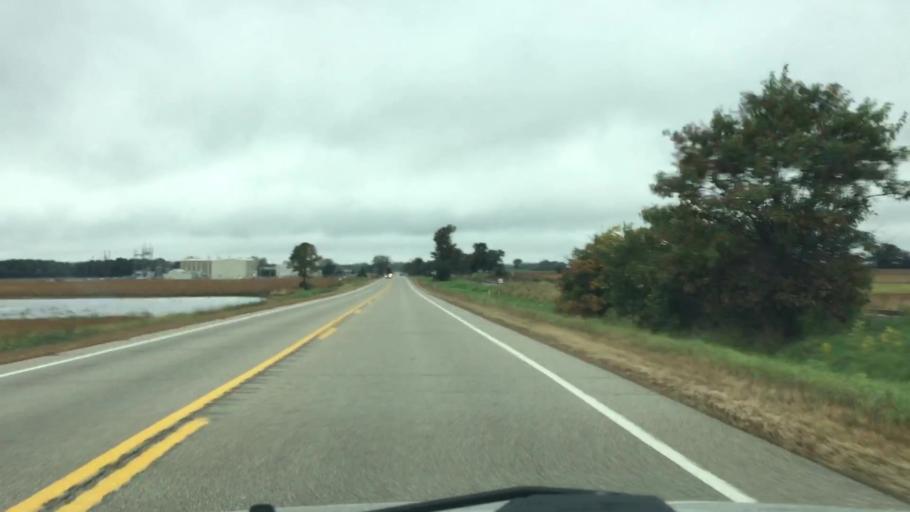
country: US
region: Wisconsin
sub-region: Walworth County
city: Whitewater
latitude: 42.8014
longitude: -88.7957
